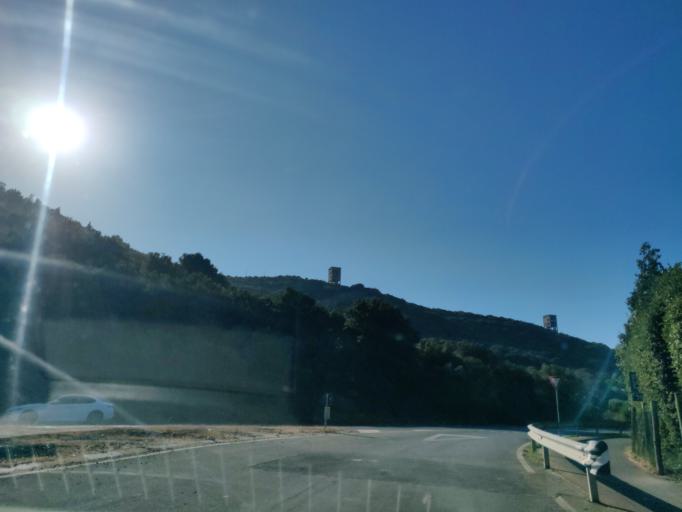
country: IT
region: Tuscany
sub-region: Provincia di Grosseto
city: Porto Ercole
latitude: 42.4162
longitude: 11.2047
